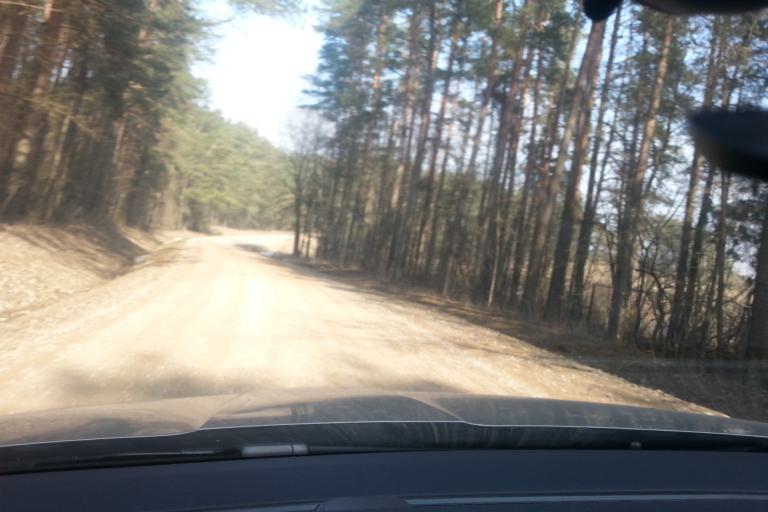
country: LT
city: Trakai
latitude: 54.5795
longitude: 24.9735
